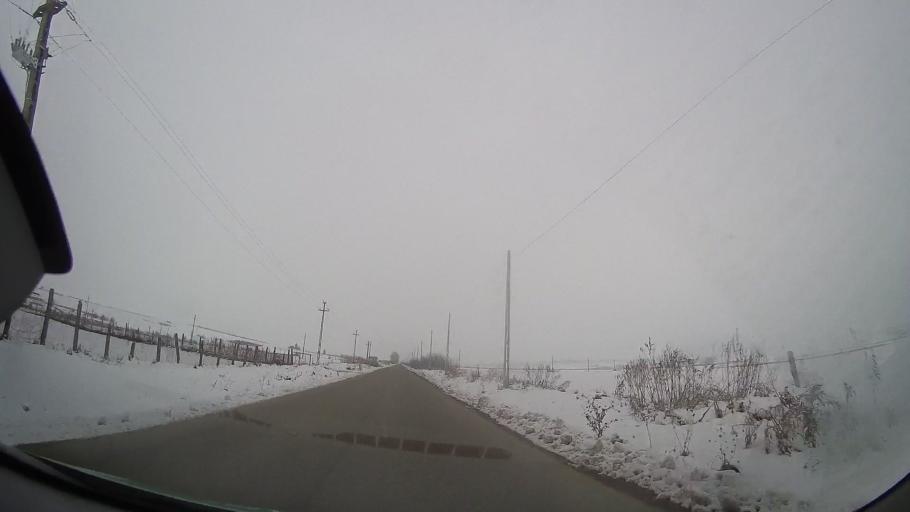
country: RO
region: Vaslui
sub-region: Comuna Todiresti
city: Todiresti
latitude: 46.8406
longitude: 27.3979
